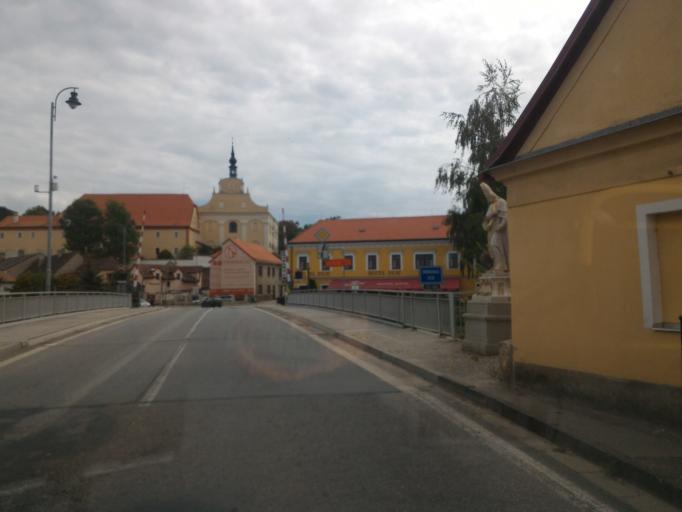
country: CZ
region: Jihocesky
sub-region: Okres Jindrichuv Hradec
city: Dacice
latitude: 49.0783
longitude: 15.4386
